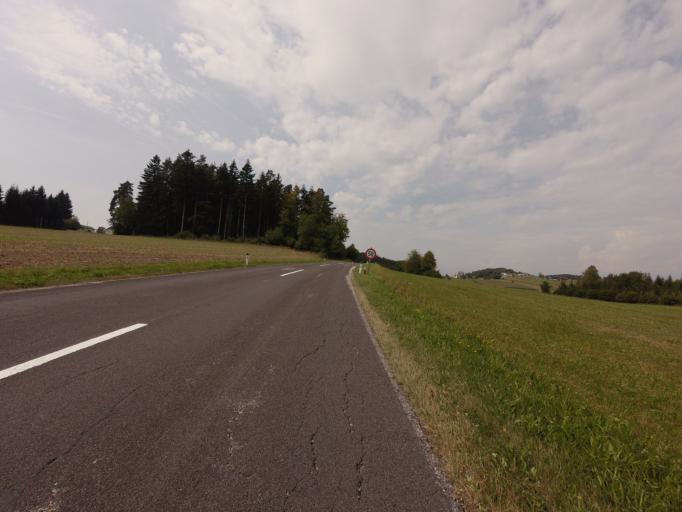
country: AT
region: Upper Austria
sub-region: Politischer Bezirk Urfahr-Umgebung
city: Reichenthal
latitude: 48.5522
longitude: 14.4238
